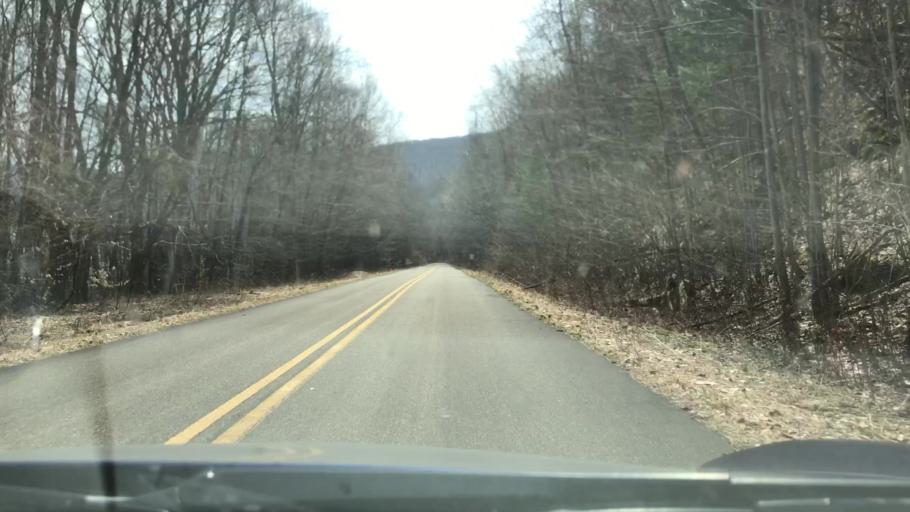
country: US
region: Pennsylvania
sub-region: Warren County
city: Sheffield
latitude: 41.8257
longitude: -78.9561
